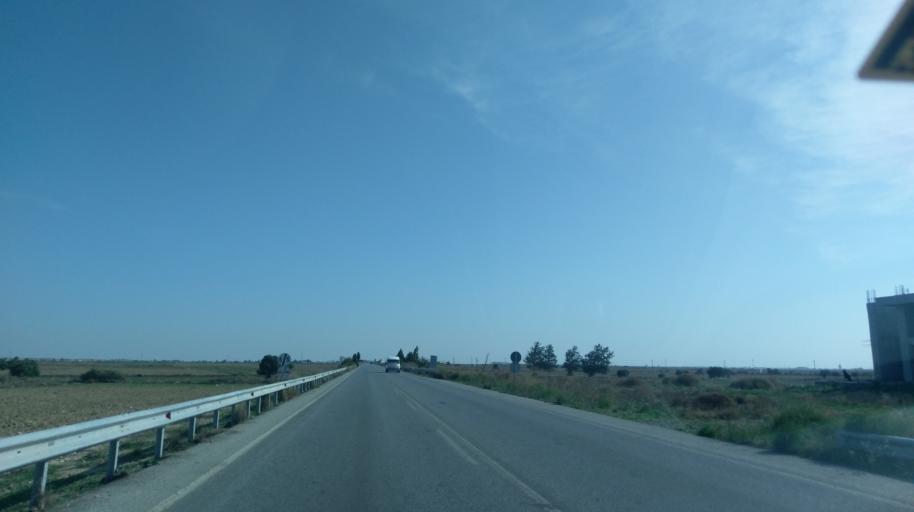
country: CY
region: Ammochostos
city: Lefkonoiko
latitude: 35.2569
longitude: 33.6900
